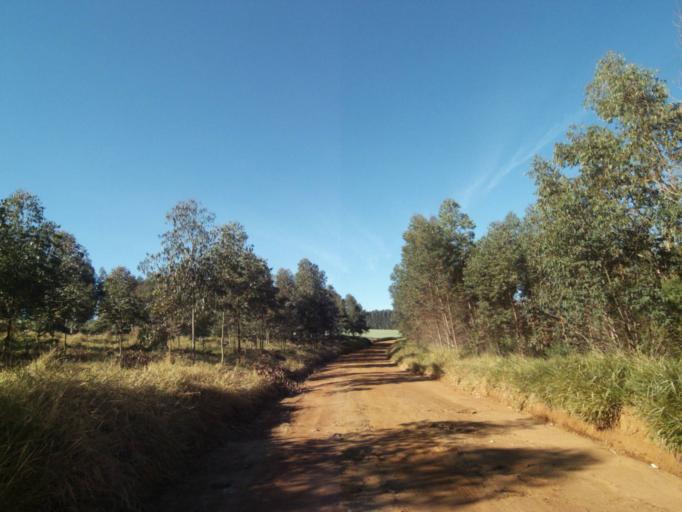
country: BR
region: Parana
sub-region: Tibagi
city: Tibagi
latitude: -24.5390
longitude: -50.3685
